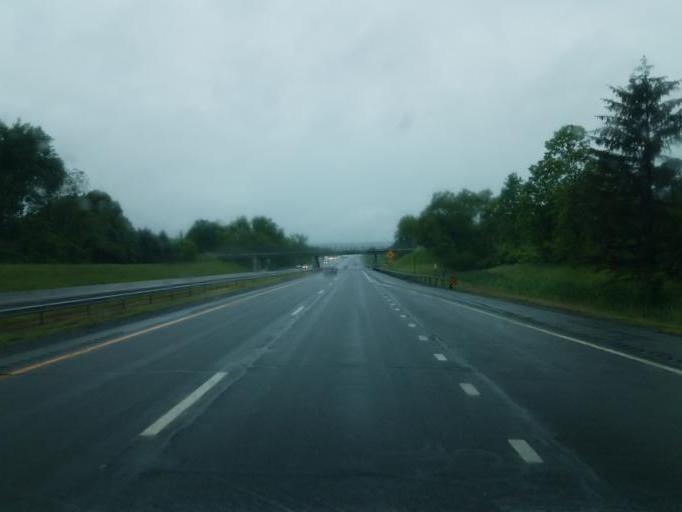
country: US
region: New York
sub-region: Madison County
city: Oneida
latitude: 43.1147
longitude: -75.6503
